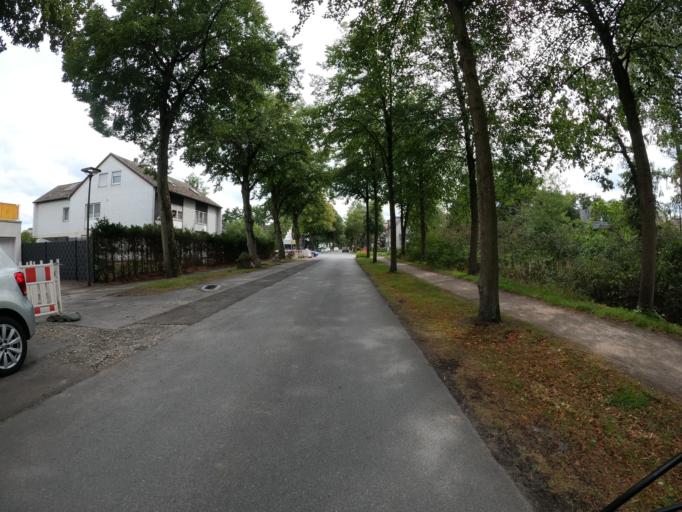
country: DE
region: North Rhine-Westphalia
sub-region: Regierungsbezirk Arnsberg
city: Lippstadt
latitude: 51.7108
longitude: 8.3373
